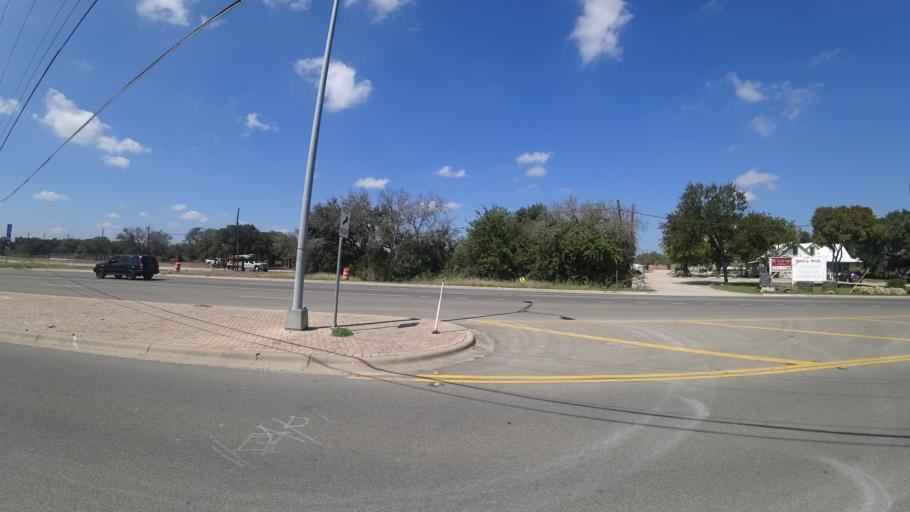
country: US
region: Texas
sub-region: Williamson County
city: Brushy Creek
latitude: 30.4824
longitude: -97.7425
